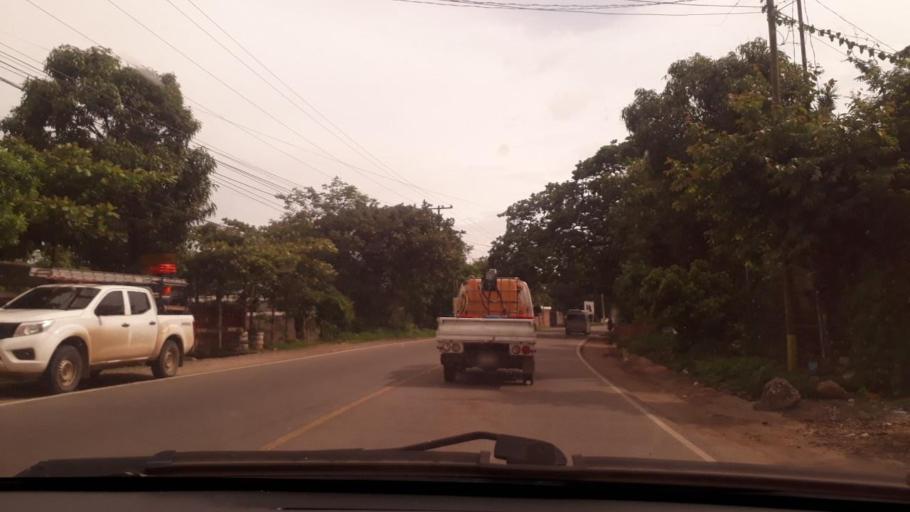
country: GT
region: Jutiapa
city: Jutiapa
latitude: 14.3026
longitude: -89.8721
